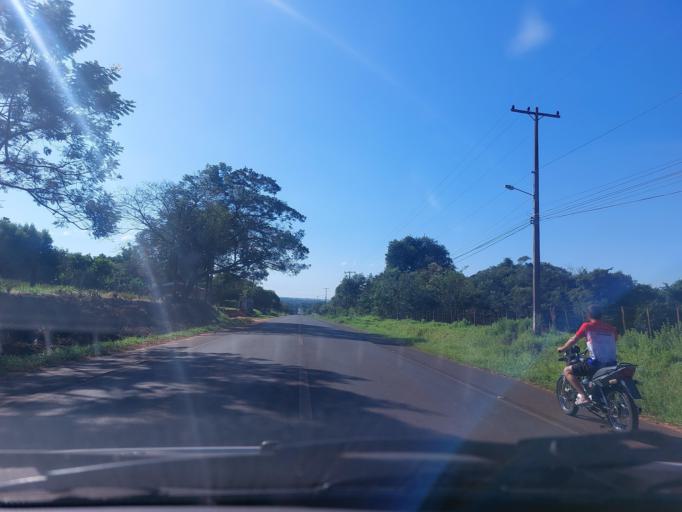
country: PY
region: San Pedro
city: Guayaybi
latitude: -24.5312
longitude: -56.4210
